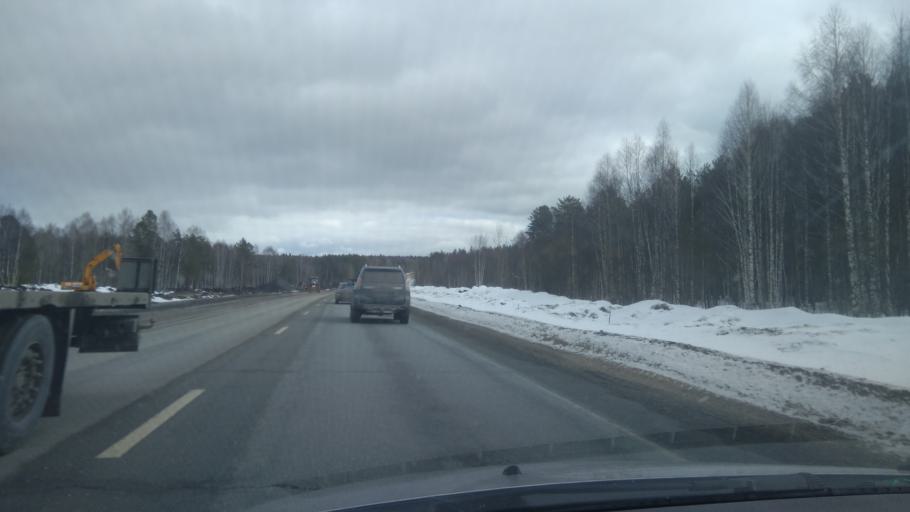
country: RU
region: Sverdlovsk
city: Bisert'
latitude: 56.8351
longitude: 58.9179
